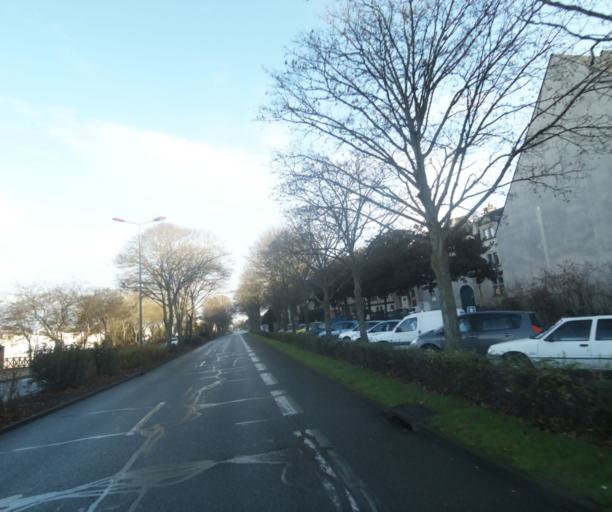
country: FR
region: Pays de la Loire
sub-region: Departement de la Sarthe
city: Le Mans
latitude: 48.0070
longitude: 0.1930
